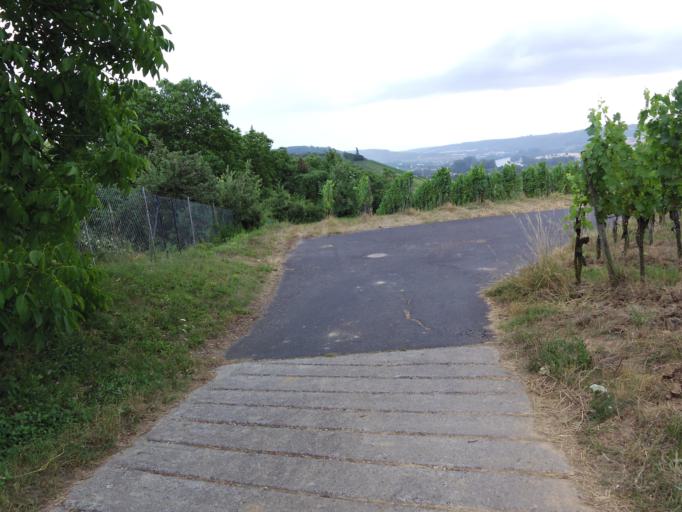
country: DE
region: Bavaria
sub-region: Regierungsbezirk Unterfranken
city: Randersacker
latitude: 49.7640
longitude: 9.9801
